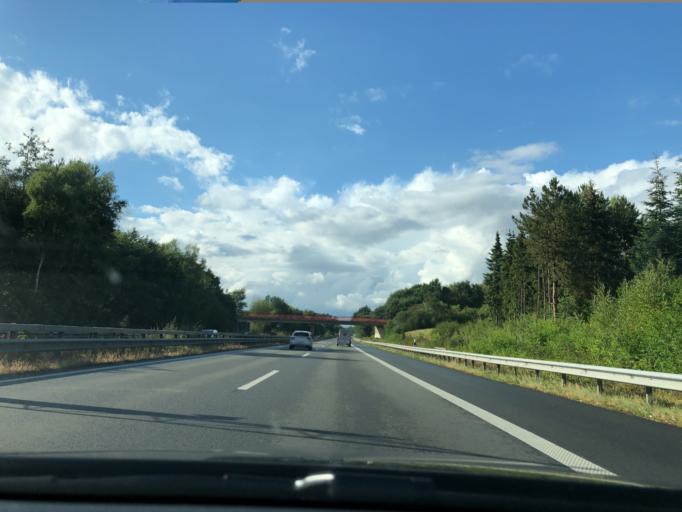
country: DE
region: Lower Saxony
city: Bad Zwischenahn
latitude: 53.2279
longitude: 8.0364
